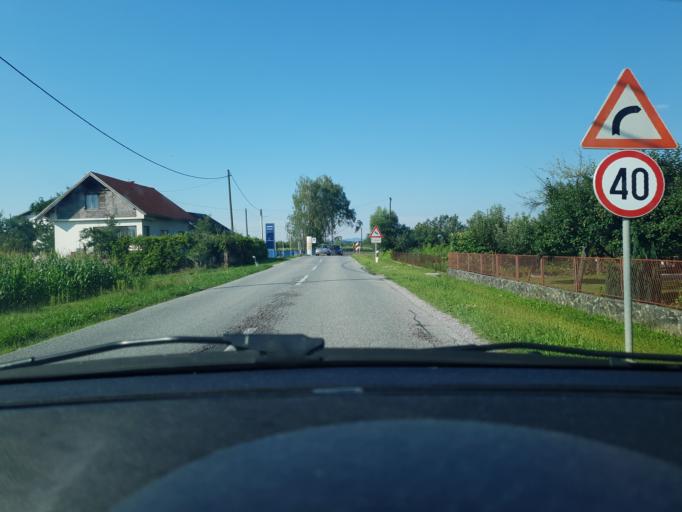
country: HR
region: Zagrebacka
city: Jakovlje
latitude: 45.9752
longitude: 15.8584
